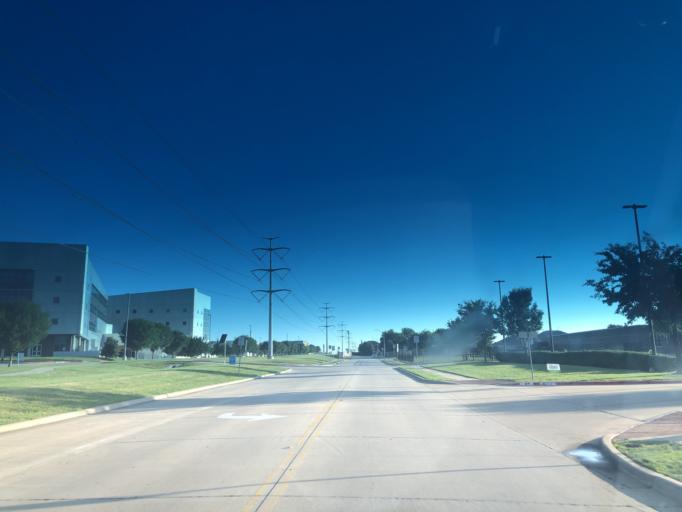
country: US
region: Texas
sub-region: Dallas County
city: Grand Prairie
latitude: 32.6989
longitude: -97.0222
